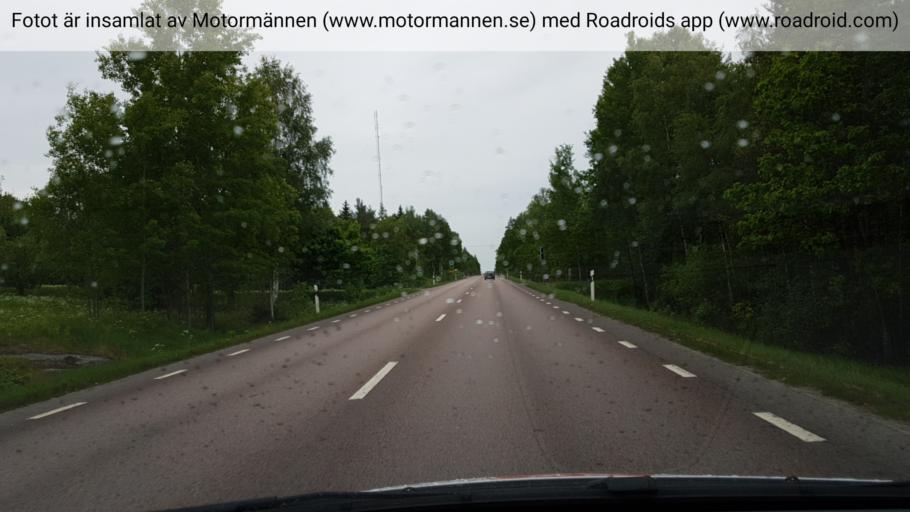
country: SE
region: Kalmar
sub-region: Hultsfreds Kommun
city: Hultsfred
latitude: 57.4562
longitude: 15.8366
